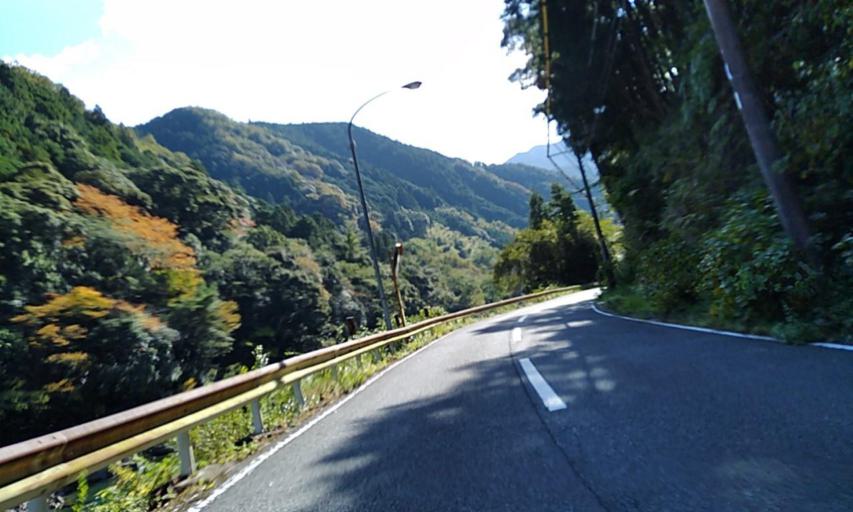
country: JP
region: Wakayama
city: Kainan
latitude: 34.0580
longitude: 135.3528
